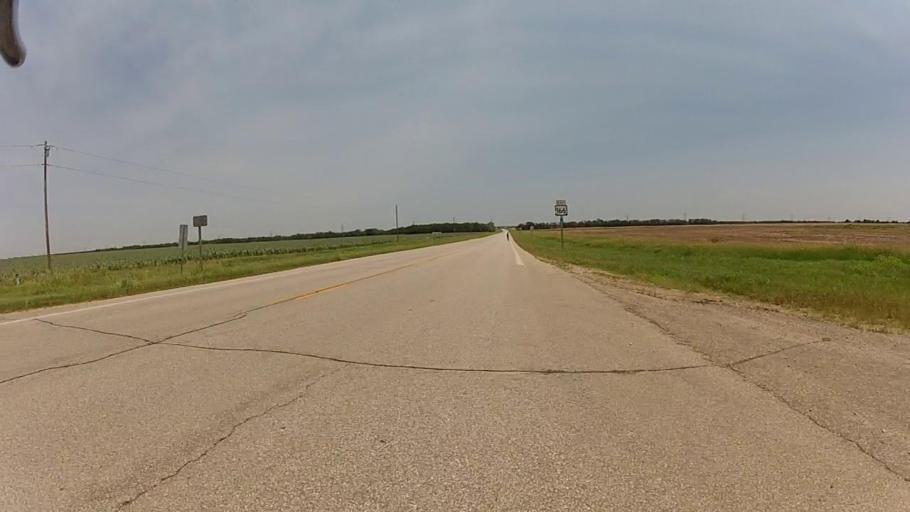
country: US
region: Kansas
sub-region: Cowley County
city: Arkansas City
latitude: 37.0564
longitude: -97.1484
